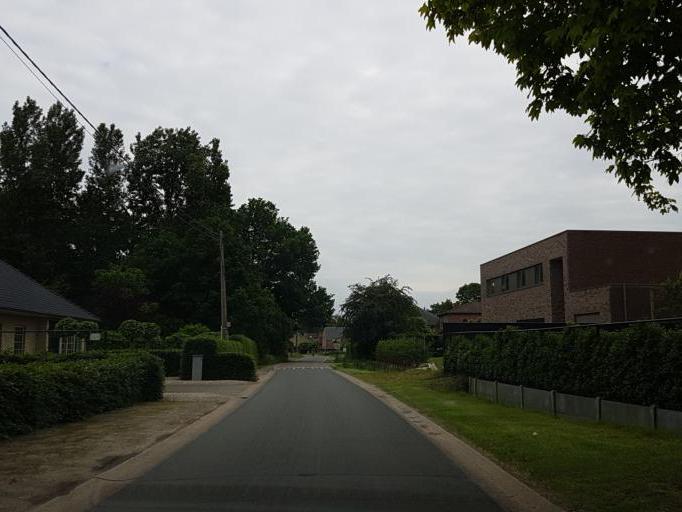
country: BE
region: Flanders
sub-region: Provincie Antwerpen
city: Zoersel
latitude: 51.2918
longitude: 4.6832
